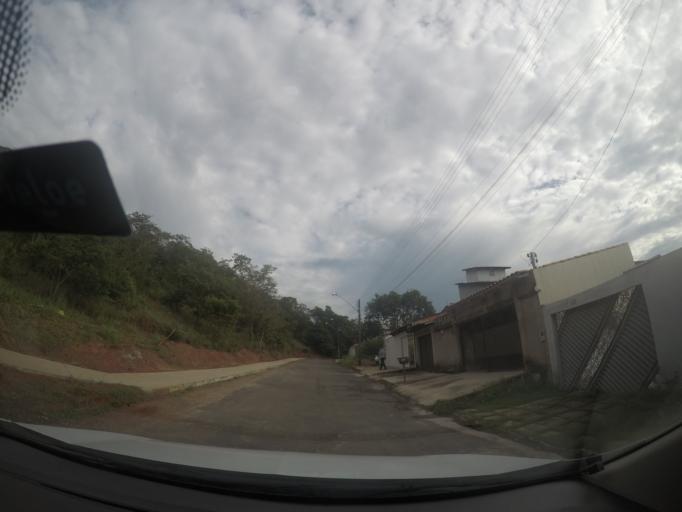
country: BR
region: Goias
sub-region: Goiania
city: Goiania
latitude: -16.6875
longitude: -49.2006
